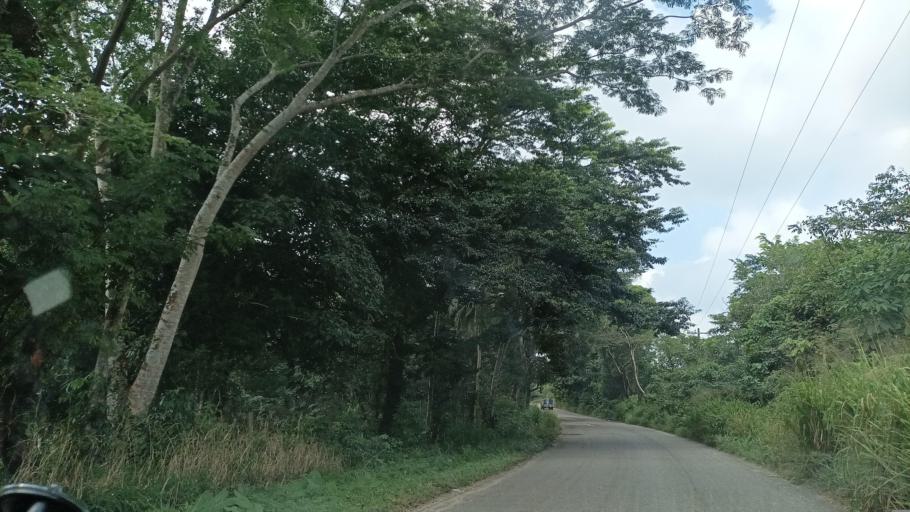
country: MX
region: Veracruz
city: Las Choapas
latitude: 17.7727
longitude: -94.1086
